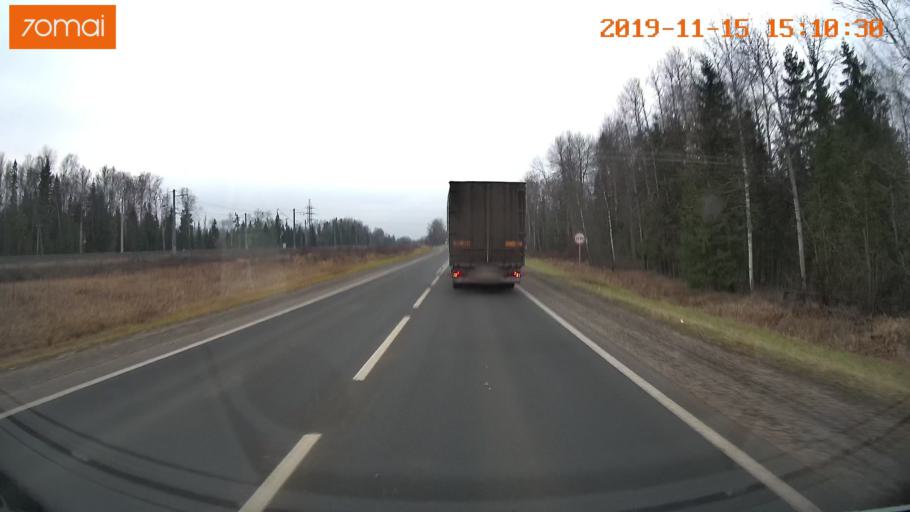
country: RU
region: Jaroslavl
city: Prechistoye
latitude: 58.3472
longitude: 40.2534
